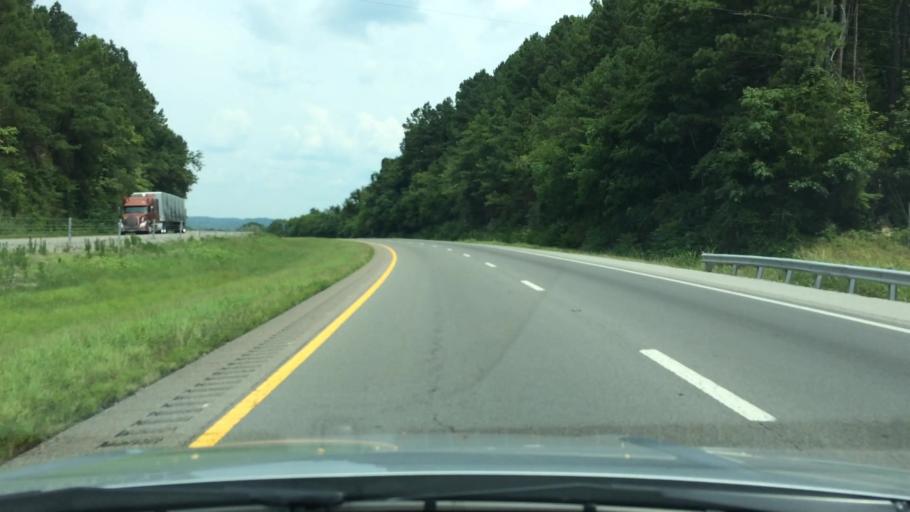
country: US
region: Tennessee
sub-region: Marshall County
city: Cornersville
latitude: 35.2603
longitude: -86.8832
